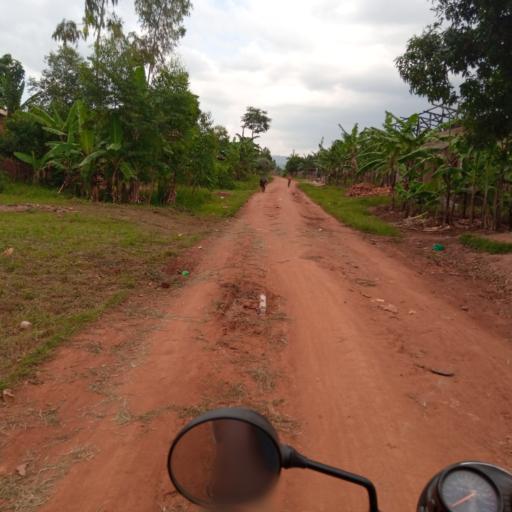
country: UG
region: Eastern Region
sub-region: Mbale District
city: Mbale
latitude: 1.1204
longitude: 34.1790
